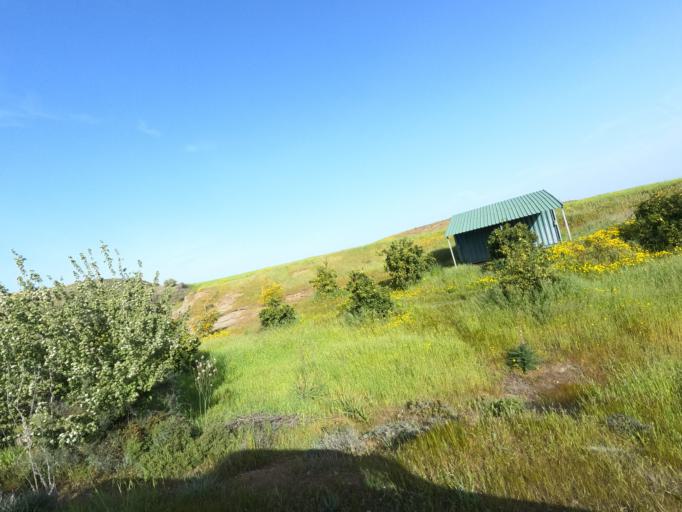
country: CY
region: Lefkosia
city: Lefka
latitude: 35.0879
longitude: 32.9408
